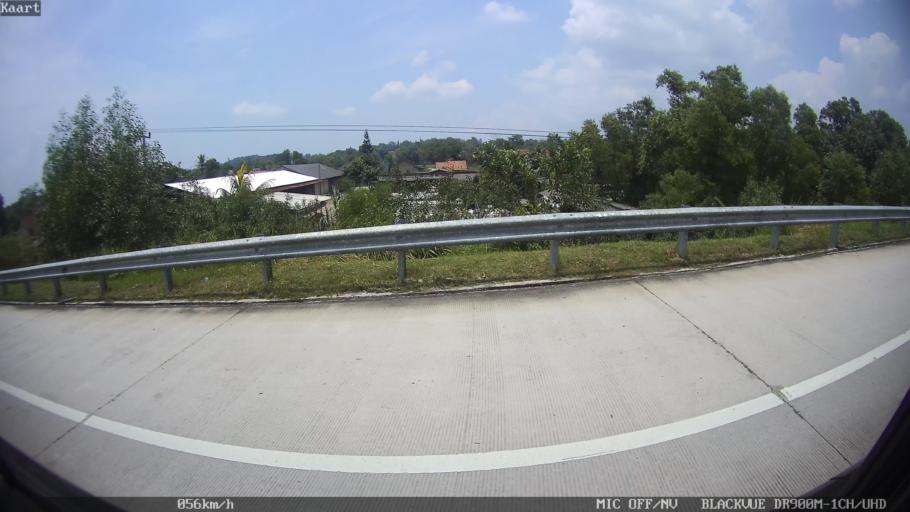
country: ID
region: Lampung
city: Natar
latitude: -5.2812
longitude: 105.1995
